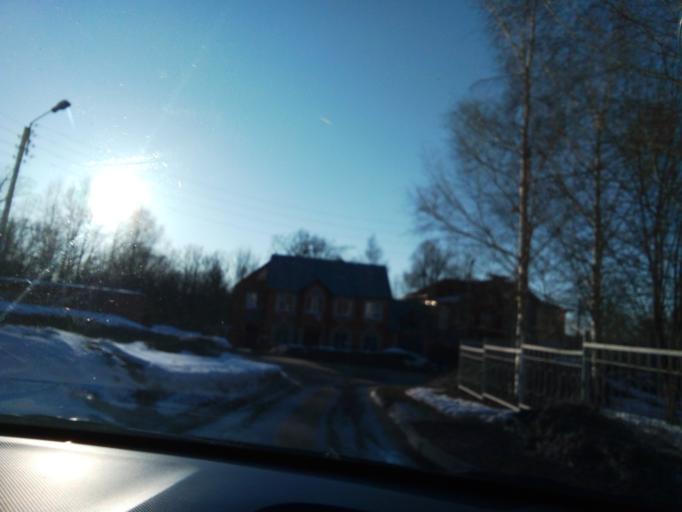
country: RU
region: Chuvashia
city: Novyye Lapsary
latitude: 56.1376
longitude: 47.1554
